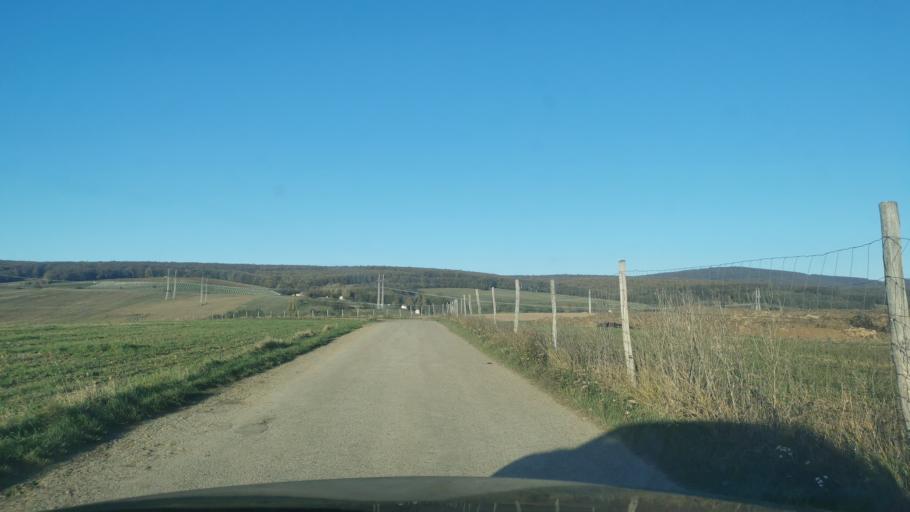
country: CZ
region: South Moravian
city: Sudomerice
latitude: 48.7911
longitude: 17.3019
